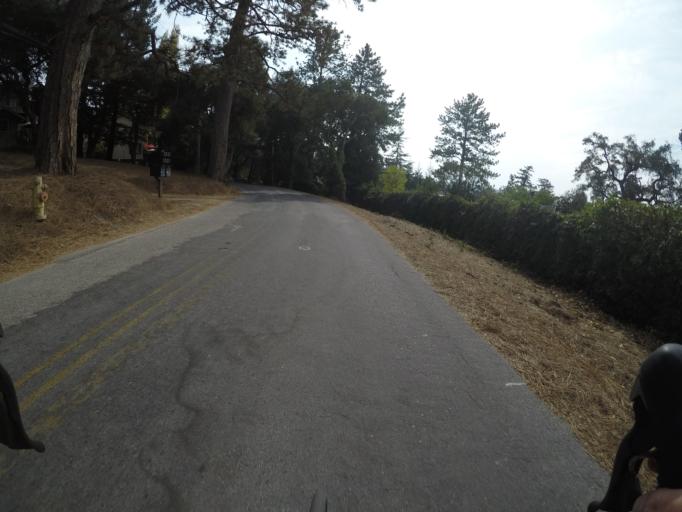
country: US
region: California
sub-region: Santa Cruz County
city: Scotts Valley
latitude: 37.0515
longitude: -122.0248
